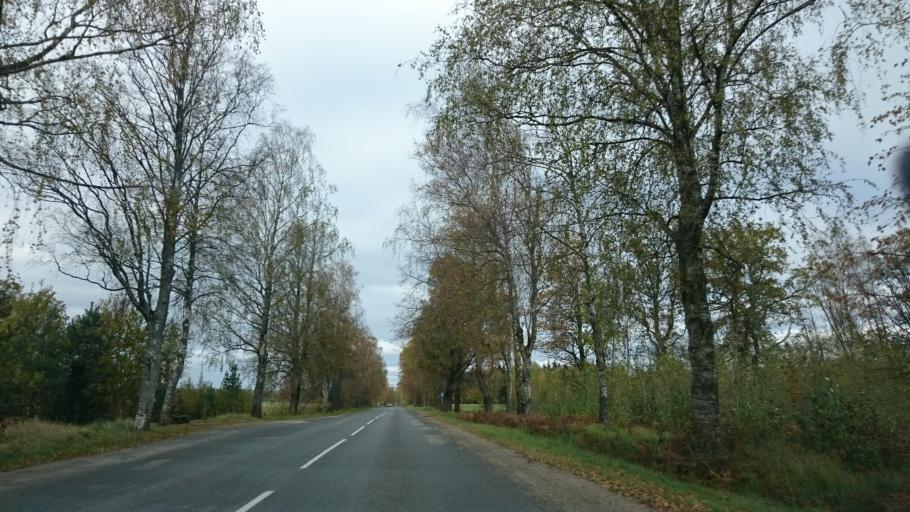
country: LV
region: Amatas Novads
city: Drabesi
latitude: 57.2702
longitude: 25.2734
